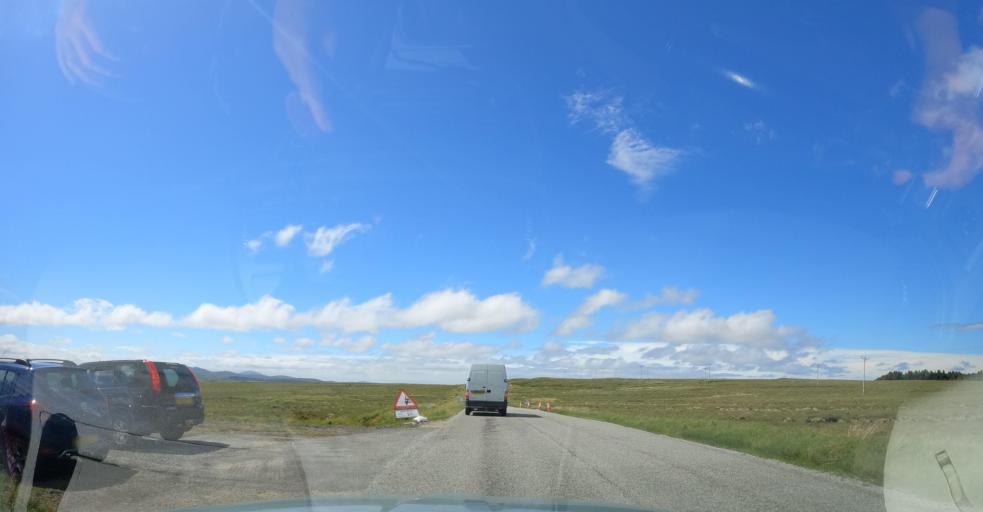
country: GB
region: Scotland
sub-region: Eilean Siar
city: Isle of Lewis
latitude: 58.1837
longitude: -6.6708
